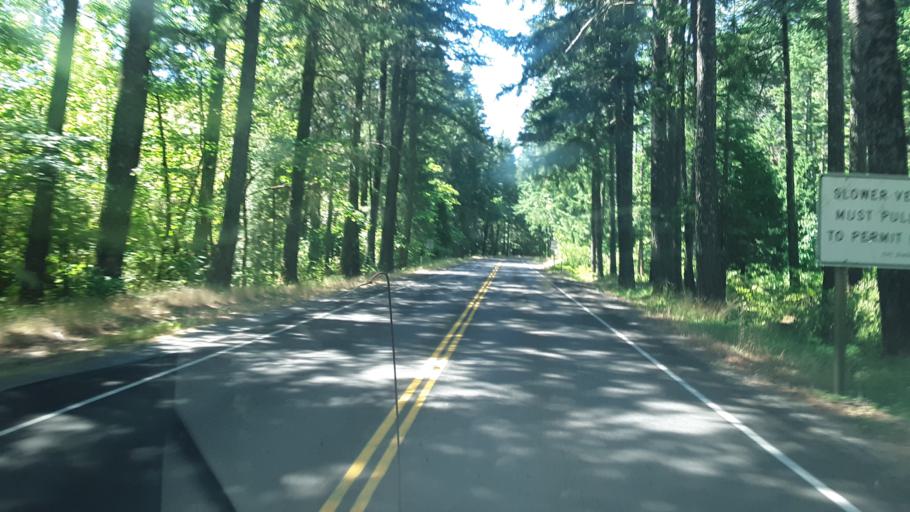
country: US
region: Oregon
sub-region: Josephine County
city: Cave Junction
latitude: 41.9866
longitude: -123.7180
